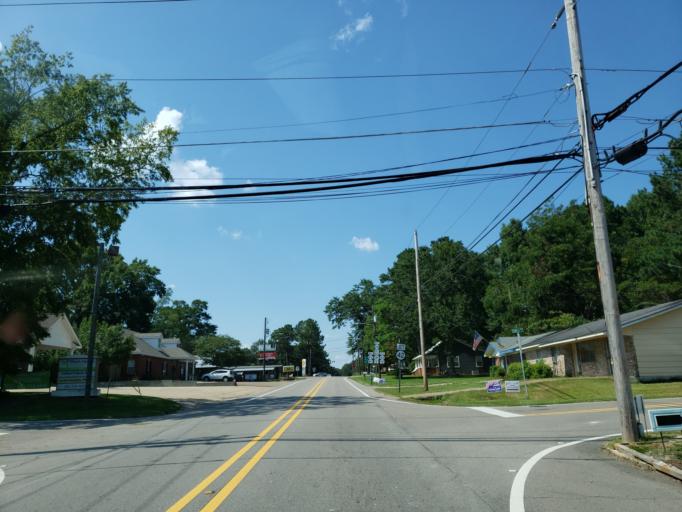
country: US
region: Mississippi
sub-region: Lamar County
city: Sumrall
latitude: 31.4174
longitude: -89.5458
